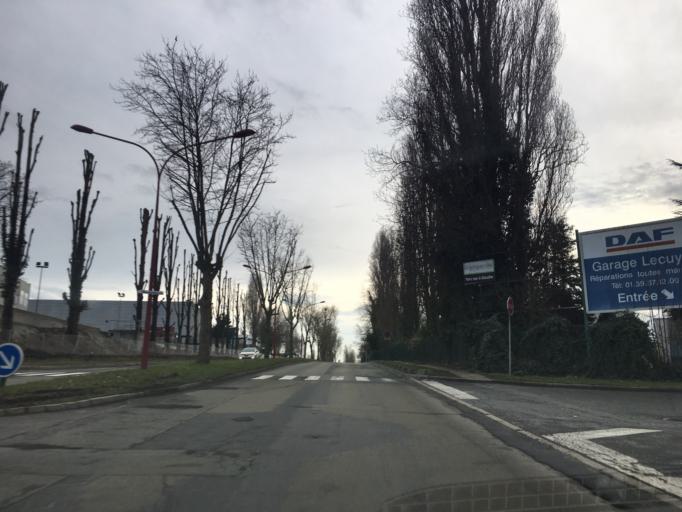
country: FR
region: Ile-de-France
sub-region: Departement du Val-d'Oise
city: Gonesse
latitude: 48.9840
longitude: 2.4584
